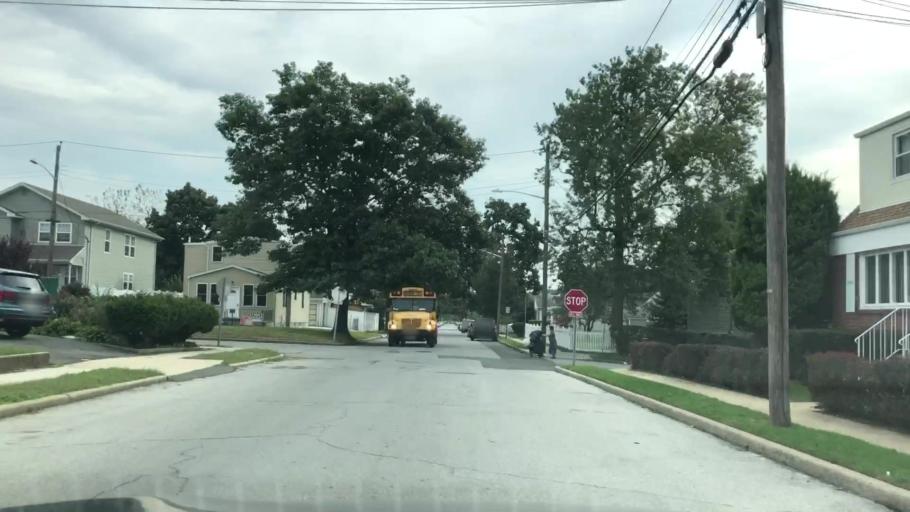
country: US
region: New York
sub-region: Nassau County
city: South Floral Park
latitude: 40.6999
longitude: -73.6919
